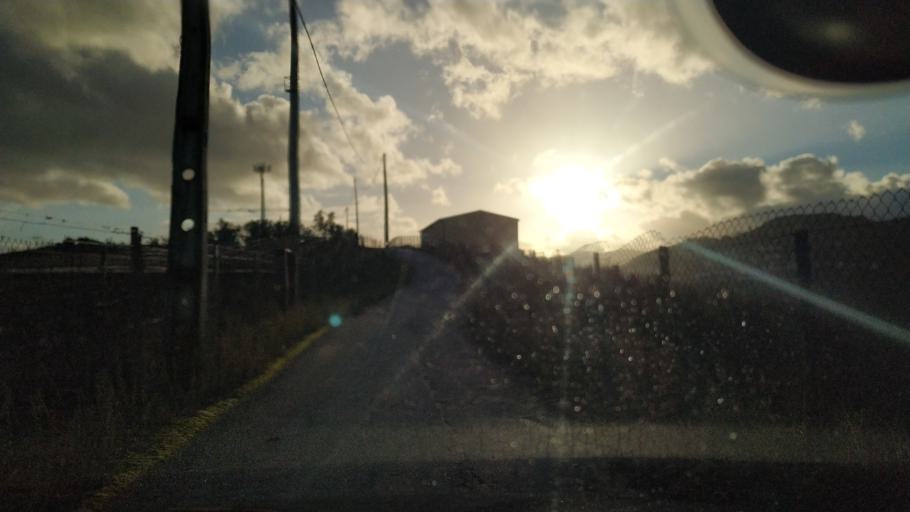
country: PT
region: Vila Real
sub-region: Vila Real
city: Vila Real
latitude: 41.2635
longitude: -7.7565
